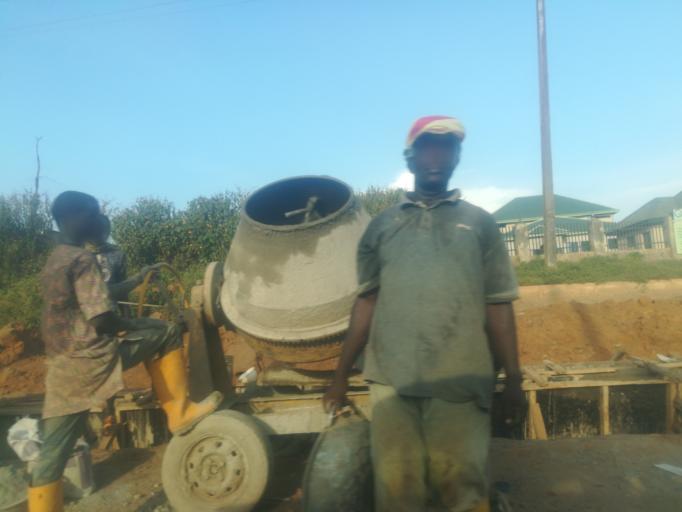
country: NG
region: Oyo
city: Moniya
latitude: 7.5457
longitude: 3.8956
